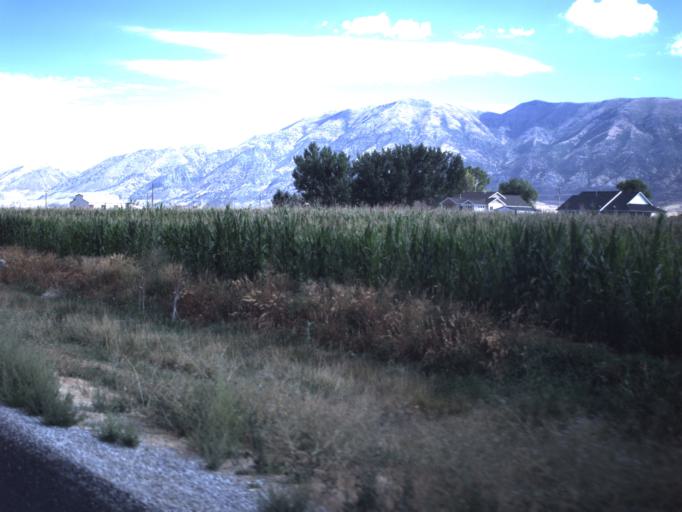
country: US
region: Utah
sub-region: Box Elder County
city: Honeyville
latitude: 41.6229
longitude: -112.1268
